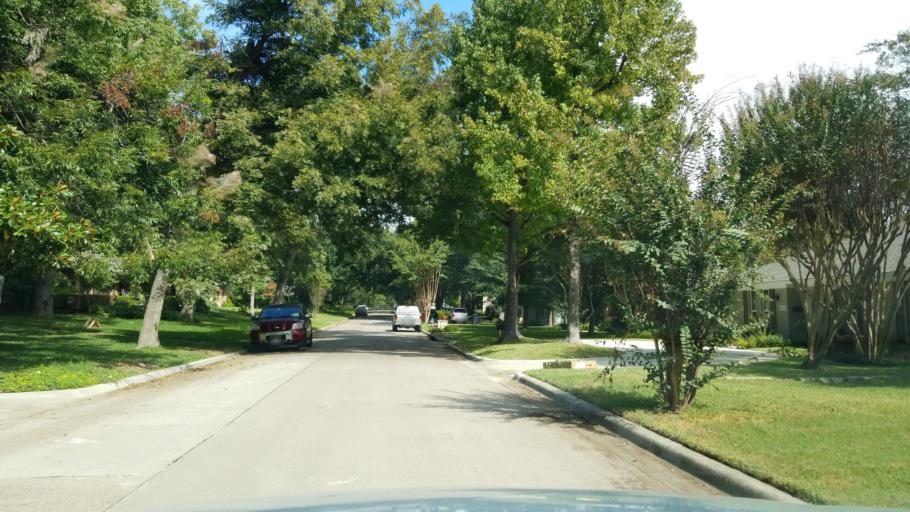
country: US
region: Texas
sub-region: Dallas County
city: Highland Park
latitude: 32.8076
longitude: -96.7175
